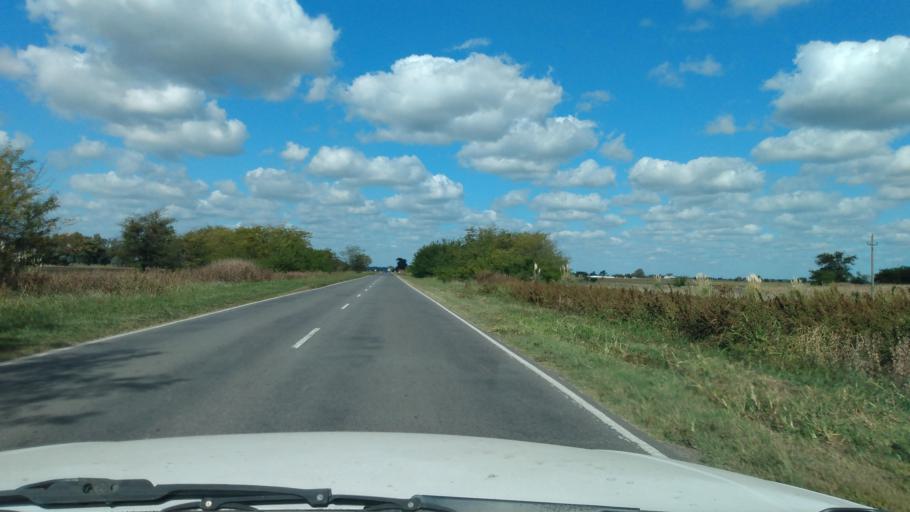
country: AR
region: Buenos Aires
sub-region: Partido de Navarro
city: Navarro
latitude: -34.9472
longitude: -59.3204
